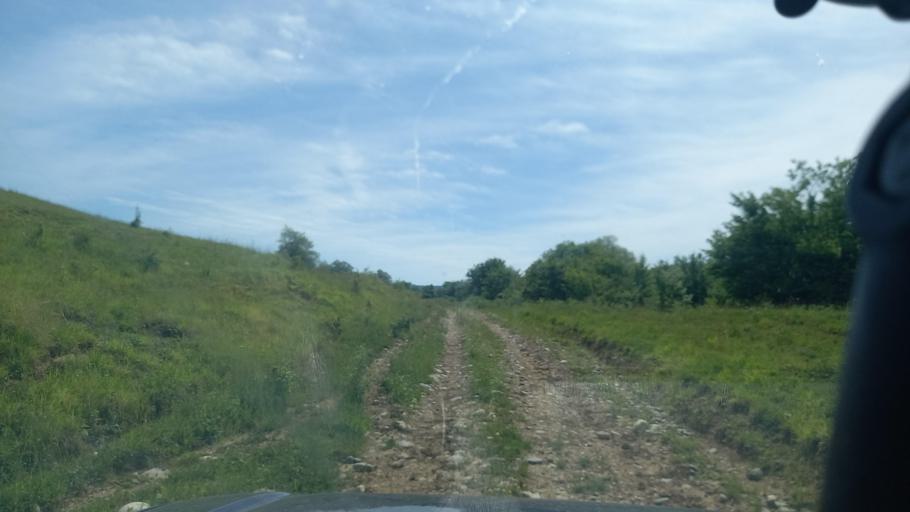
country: RU
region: Karachayevo-Cherkesiya
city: Kurdzhinovo
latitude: 44.1410
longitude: 41.0615
